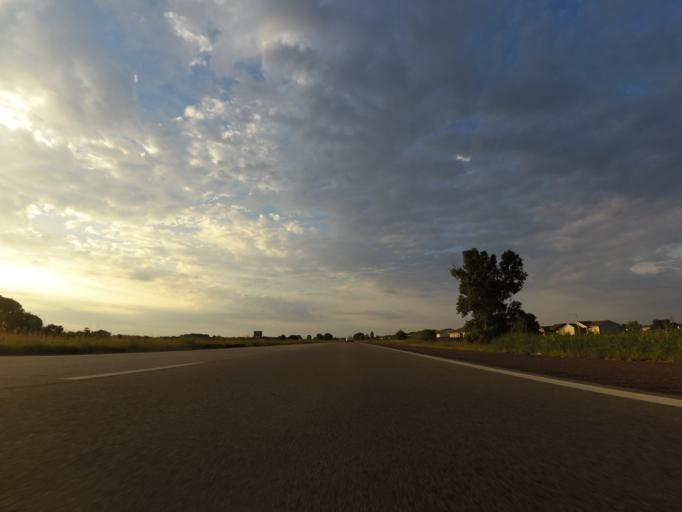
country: US
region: Kansas
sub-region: Sedgwick County
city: Maize
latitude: 37.7735
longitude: -97.4553
